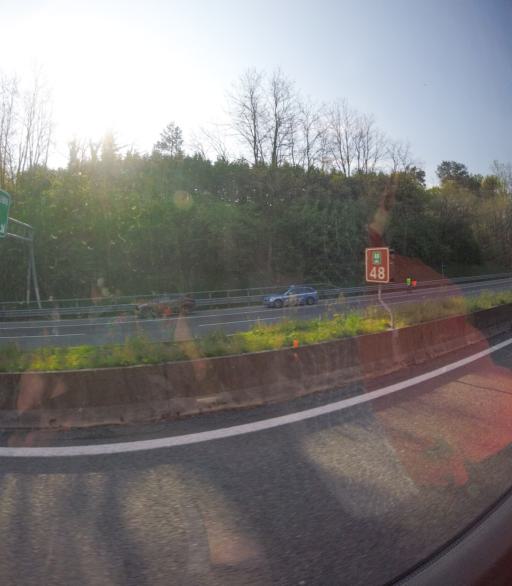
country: IT
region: Lombardy
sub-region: Provincia di Varese
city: Golasecca
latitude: 45.7164
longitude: 8.6660
